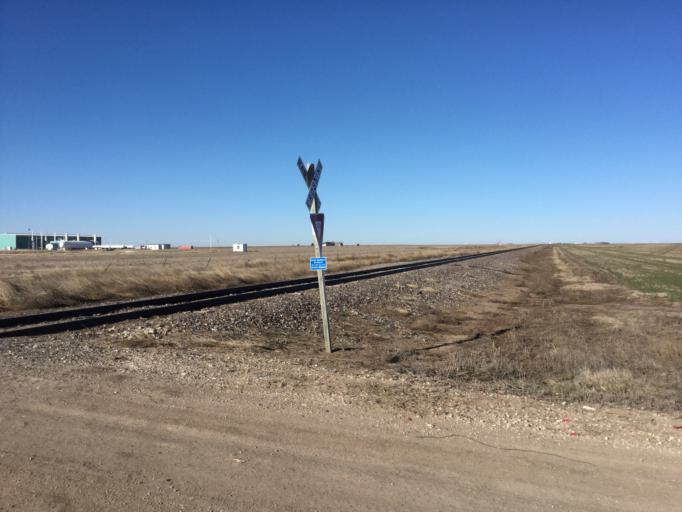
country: US
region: Kansas
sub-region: Scott County
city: Scott City
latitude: 38.4871
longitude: -100.9808
